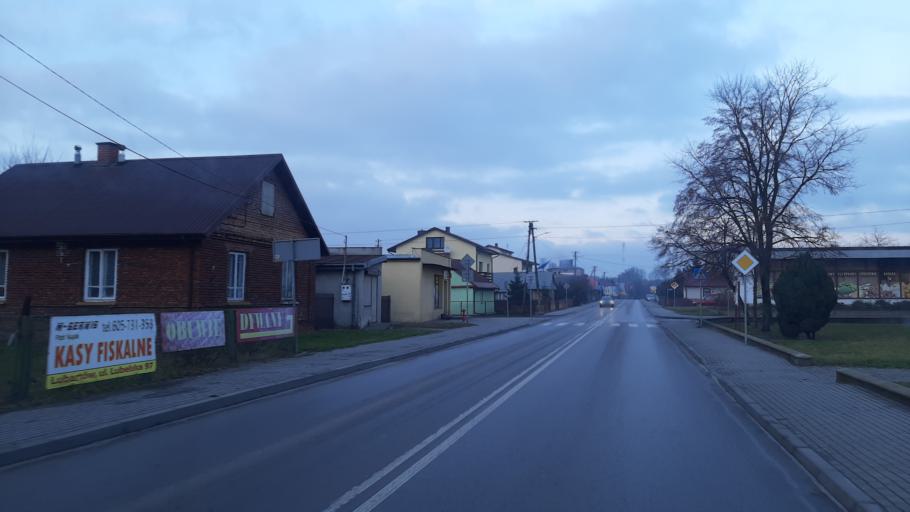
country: PL
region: Lublin Voivodeship
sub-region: Powiat lubartowski
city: Kamionka
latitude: 51.4703
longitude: 22.4621
